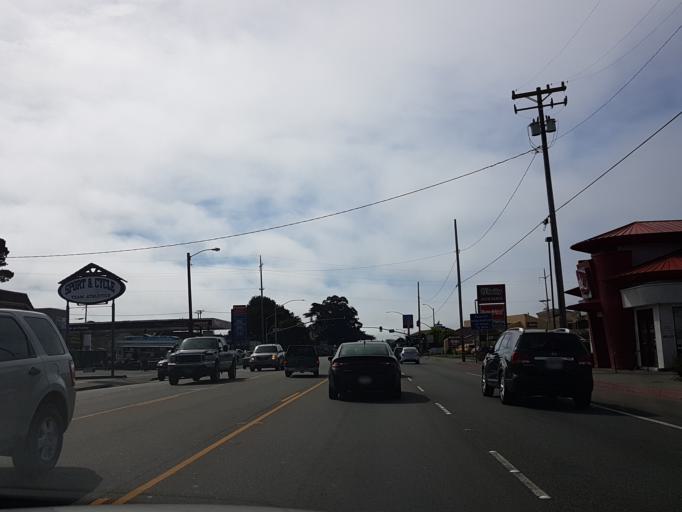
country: US
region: California
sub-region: Humboldt County
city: Eureka
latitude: 40.7928
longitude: -124.1777
